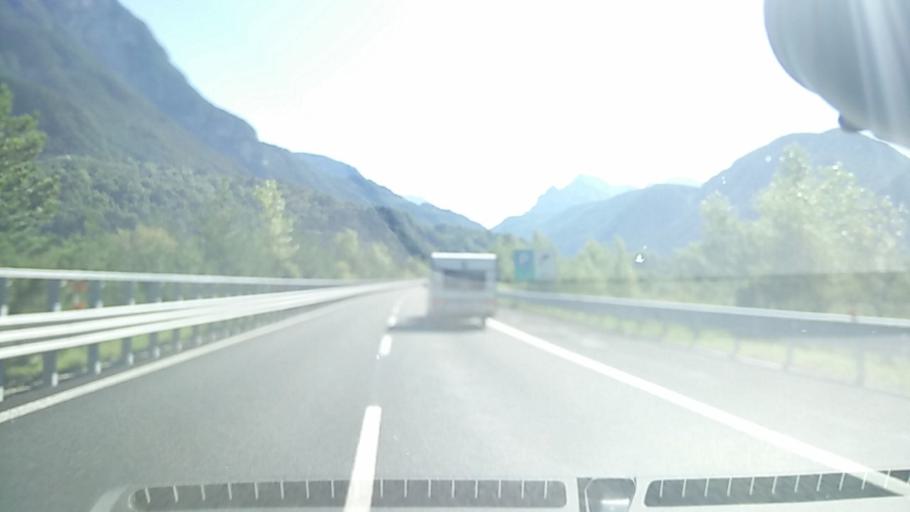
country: IT
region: Friuli Venezia Giulia
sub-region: Provincia di Udine
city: Resiutta
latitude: 46.3971
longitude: 13.2064
